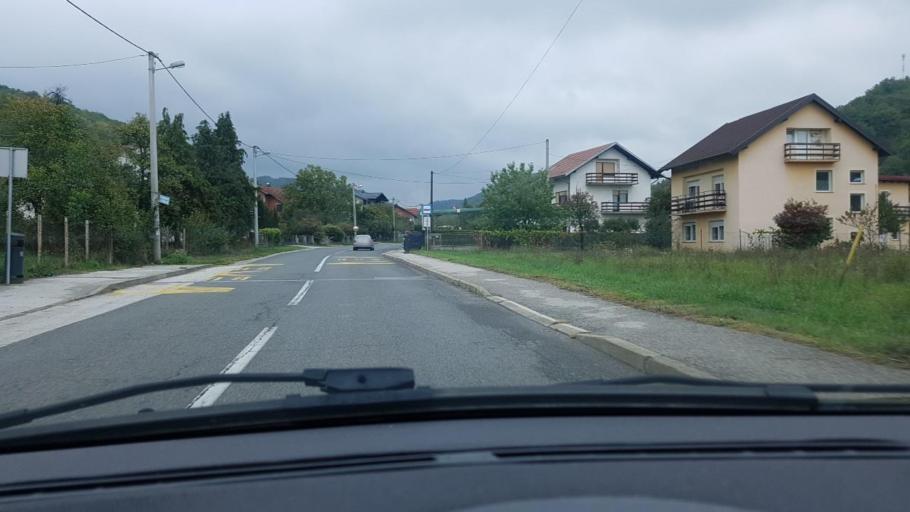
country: HR
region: Grad Zagreb
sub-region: Sesvete
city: Sesvete
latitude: 45.9146
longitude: 16.1239
